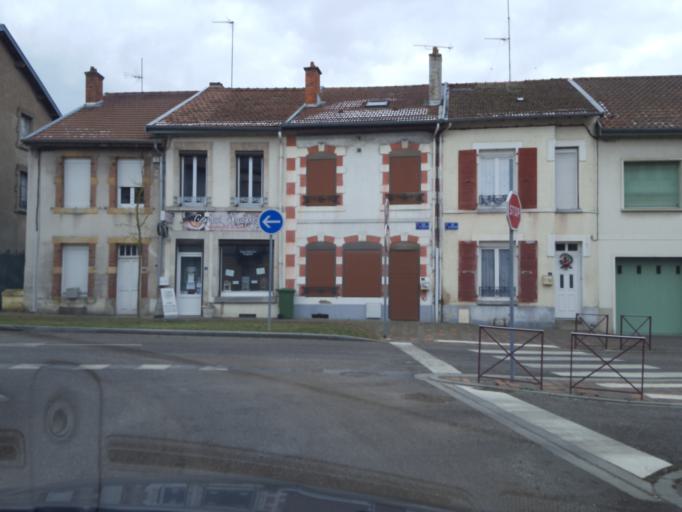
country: FR
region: Lorraine
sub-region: Departement de la Meuse
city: Etain
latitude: 49.2123
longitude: 5.6348
